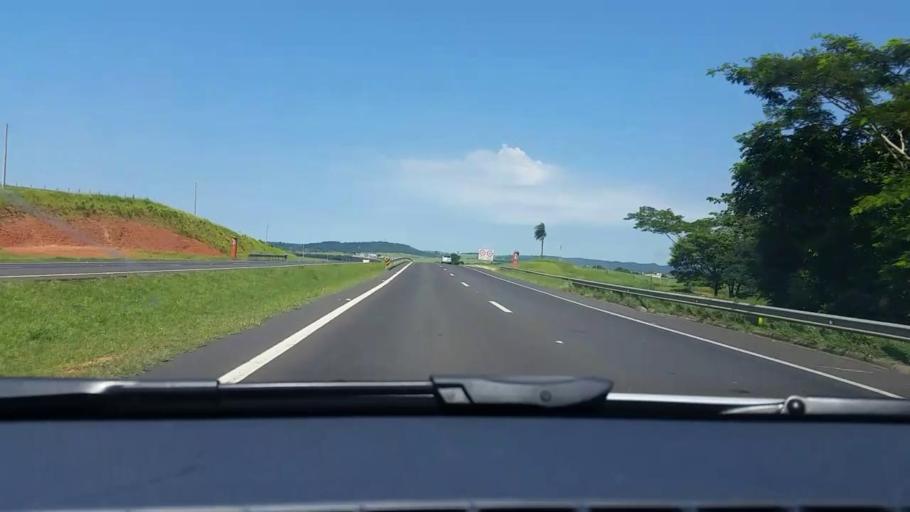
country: BR
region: Sao Paulo
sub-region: Bauru
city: Bauru
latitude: -22.3939
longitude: -49.0823
